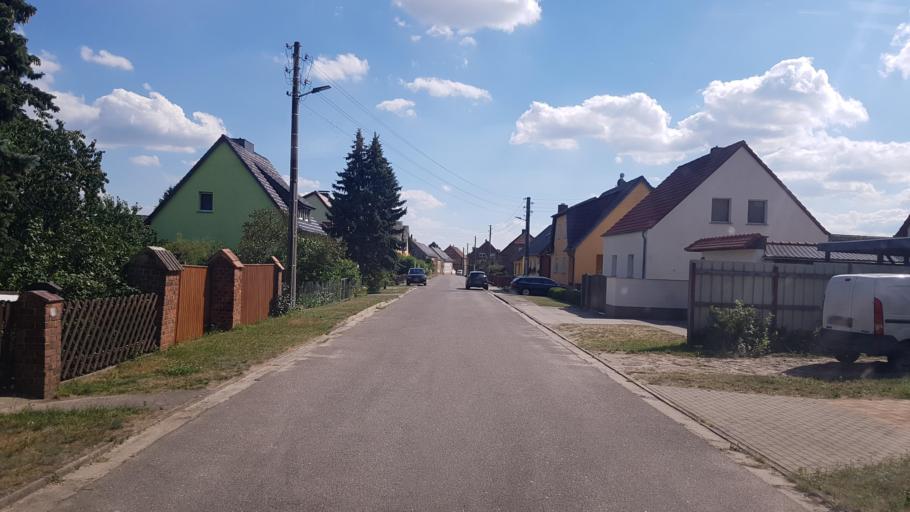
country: DE
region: Saxony-Anhalt
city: Holzdorf
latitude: 51.8594
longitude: 13.1059
